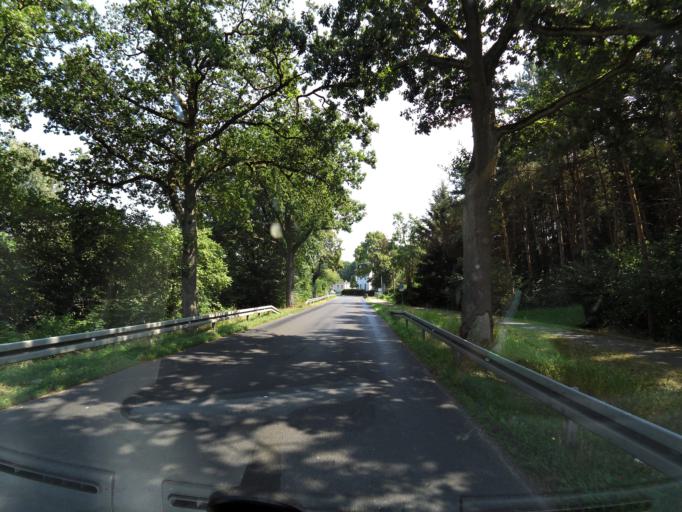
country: DE
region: Brandenburg
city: Oranienburg
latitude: 52.8244
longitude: 13.2683
